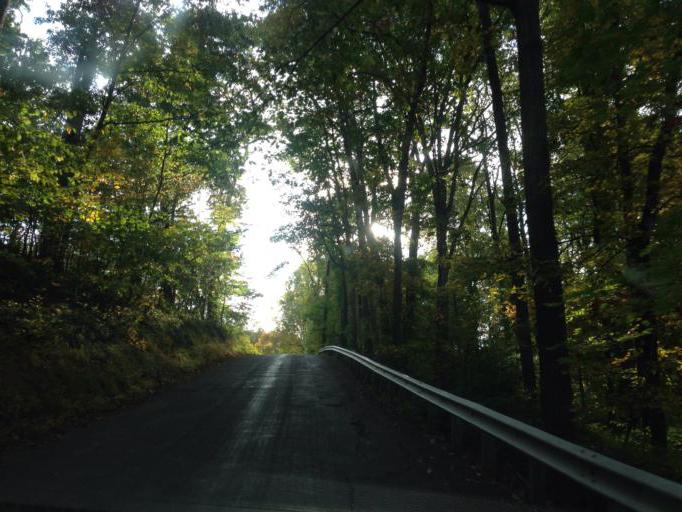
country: US
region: Maryland
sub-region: Carroll County
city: Mount Airy
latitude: 39.3228
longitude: -77.1502
